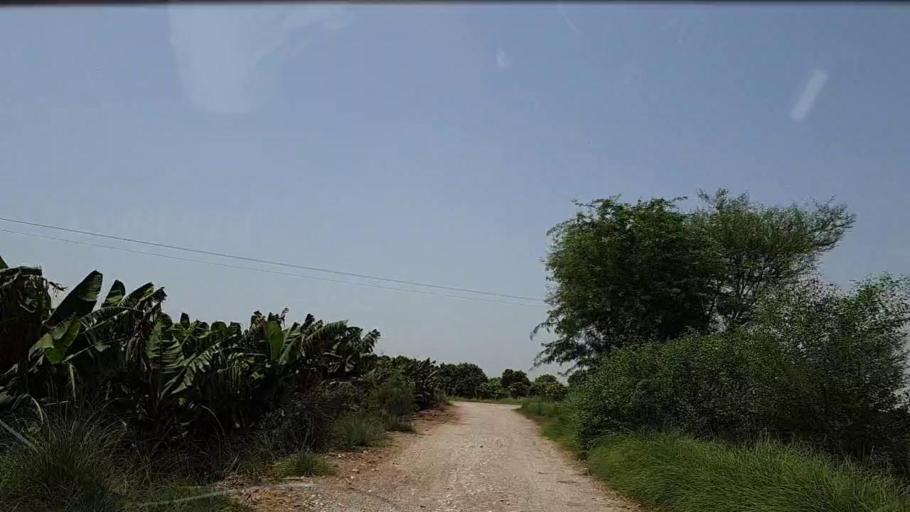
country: PK
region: Sindh
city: Tharu Shah
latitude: 26.9410
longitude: 68.0418
